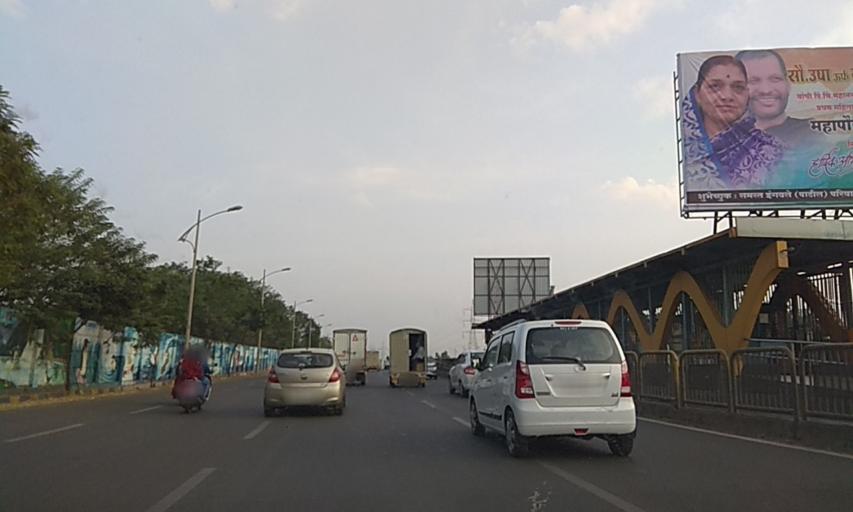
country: IN
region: Maharashtra
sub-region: Pune Division
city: Pimpri
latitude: 18.5815
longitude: 73.7985
